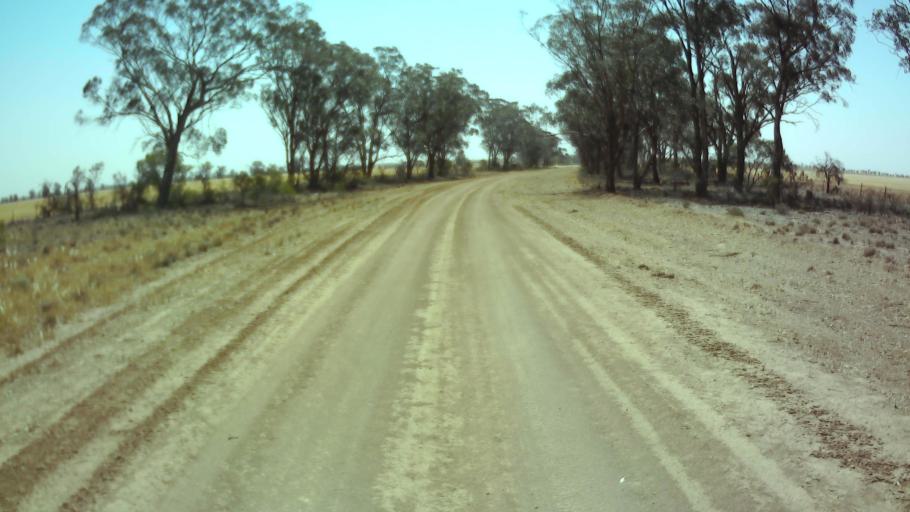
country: AU
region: New South Wales
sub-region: Weddin
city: Grenfell
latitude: -33.9210
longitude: 147.7798
